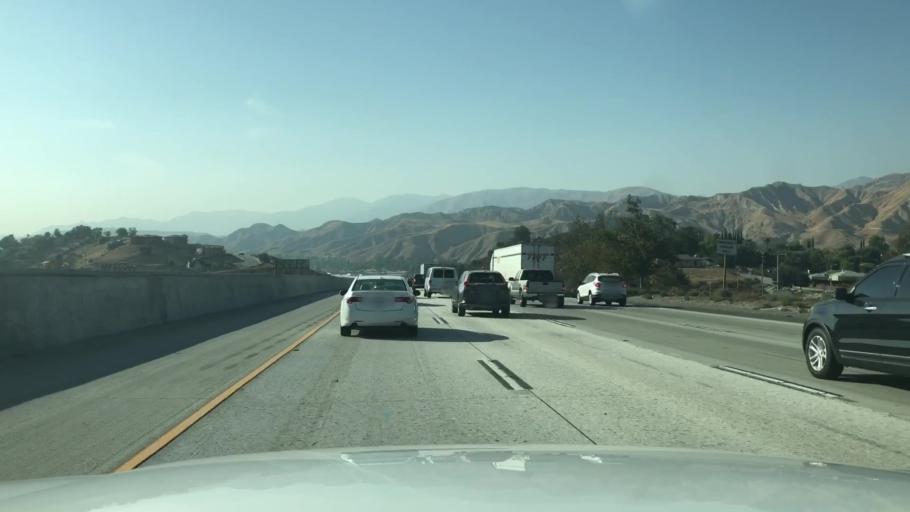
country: US
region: California
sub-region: Los Angeles County
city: Burbank
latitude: 34.2585
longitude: -118.3290
